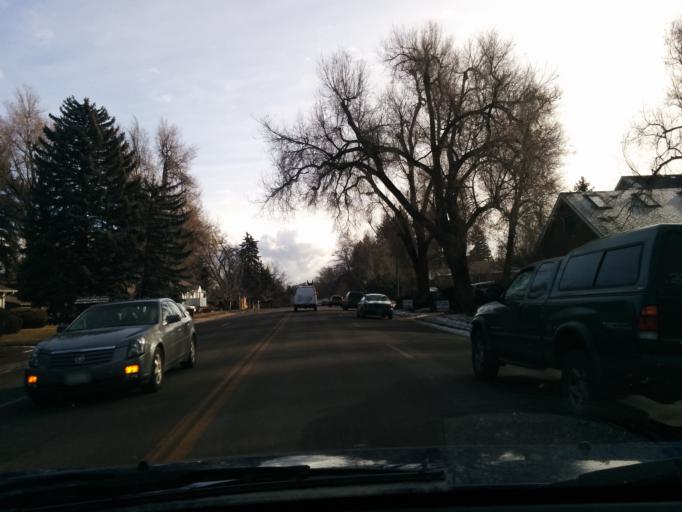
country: US
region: Colorado
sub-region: Larimer County
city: Fort Collins
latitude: 40.5671
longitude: -105.0737
